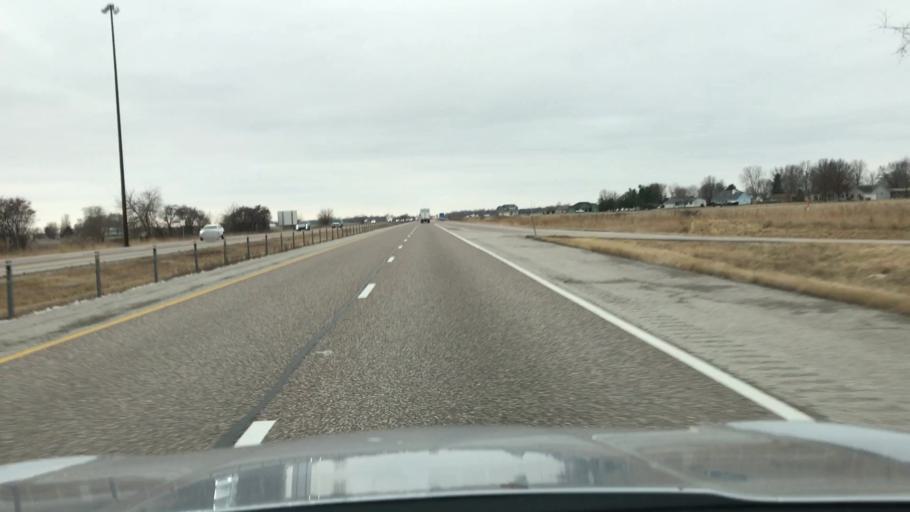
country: US
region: Illinois
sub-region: Madison County
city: Worden
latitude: 38.8872
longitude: -89.8397
